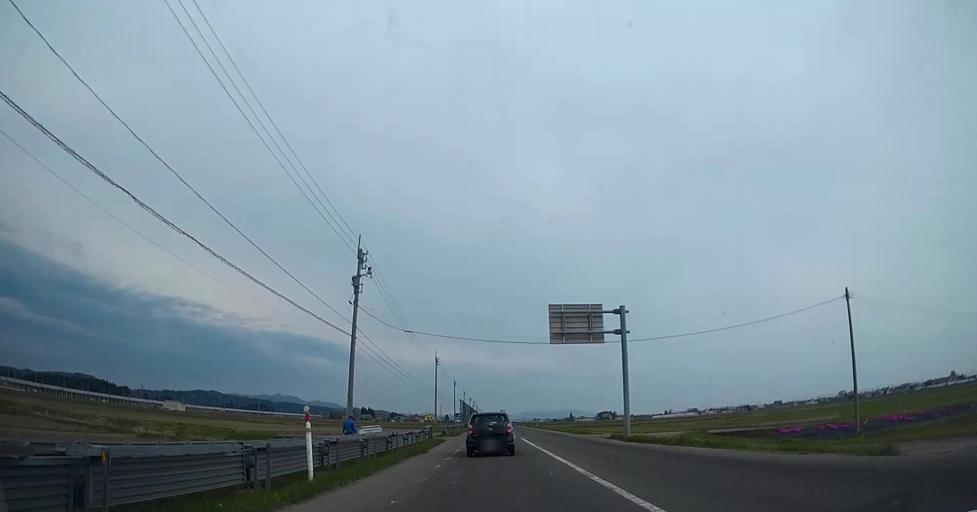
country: JP
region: Aomori
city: Aomori Shi
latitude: 40.8627
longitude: 140.6809
